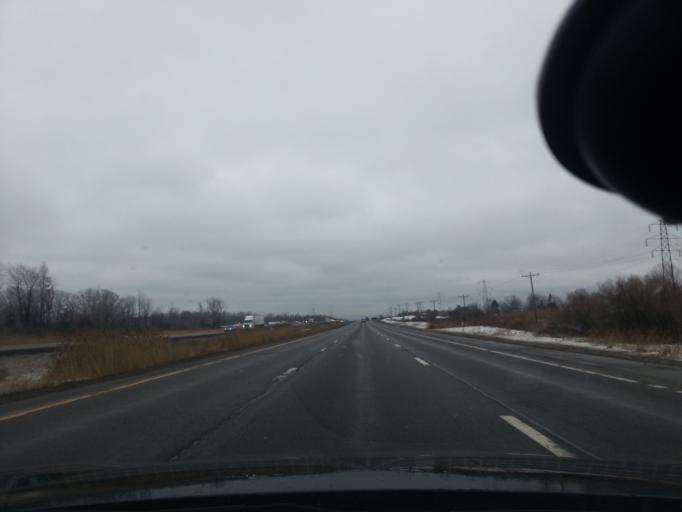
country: US
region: New York
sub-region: Onondaga County
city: Brewerton
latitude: 43.2059
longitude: -76.1275
